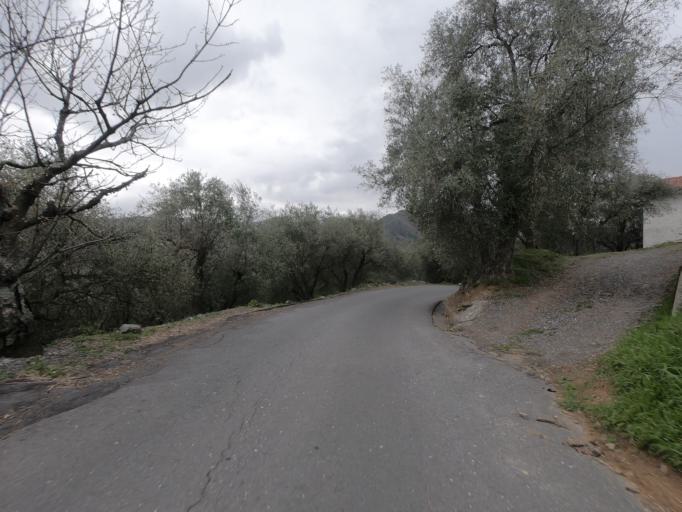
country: IT
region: Liguria
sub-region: Provincia di Savona
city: Casanova Lerrone
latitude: 44.0328
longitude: 8.0476
